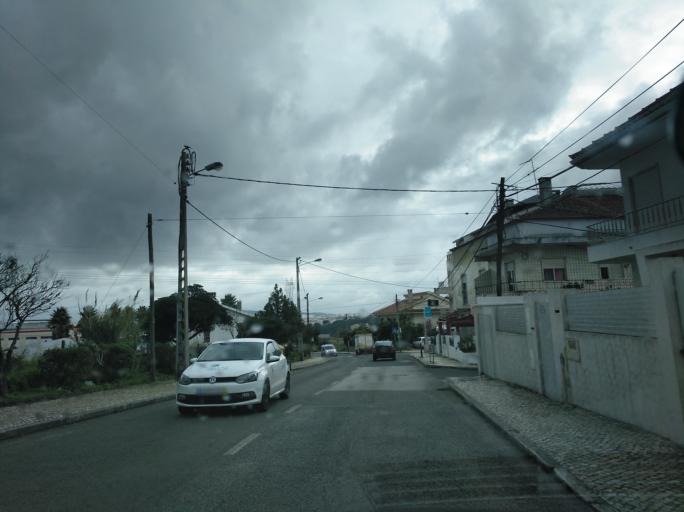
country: PT
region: Lisbon
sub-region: Odivelas
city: Famoes
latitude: 38.7878
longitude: -9.2093
